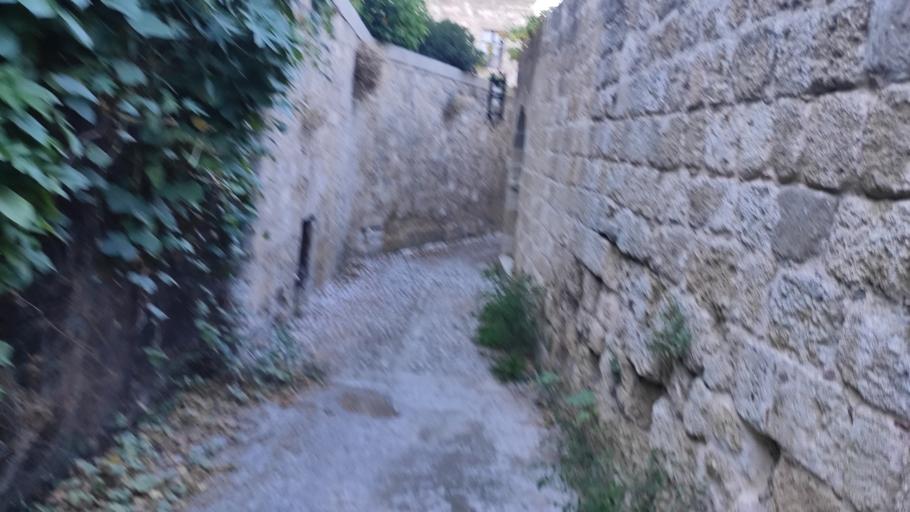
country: GR
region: South Aegean
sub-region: Nomos Dodekanisou
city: Rodos
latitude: 36.4448
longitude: 28.2248
